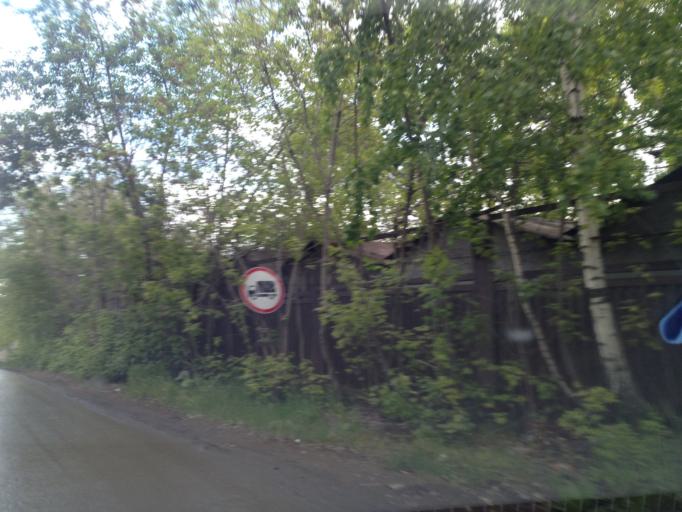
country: RU
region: Sverdlovsk
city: Yekaterinburg
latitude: 56.8456
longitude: 60.5554
